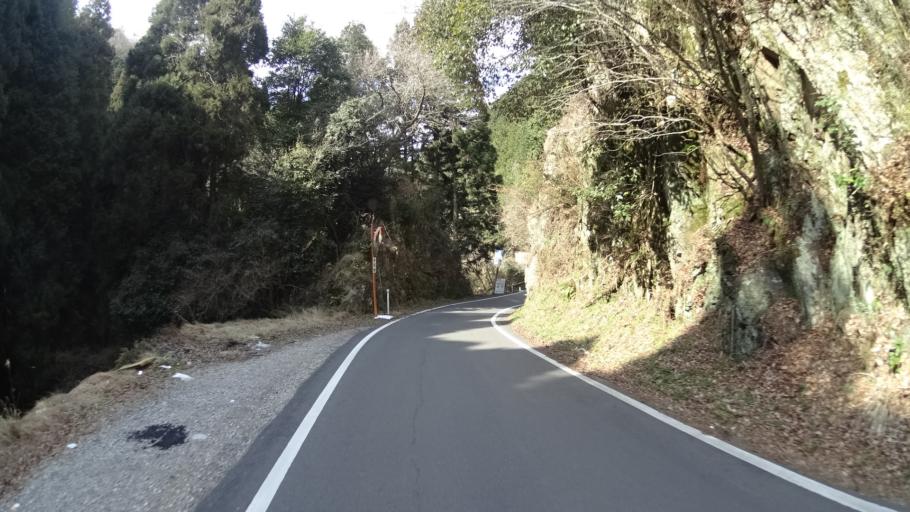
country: JP
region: Kyoto
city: Uji
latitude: 34.8192
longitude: 135.8904
